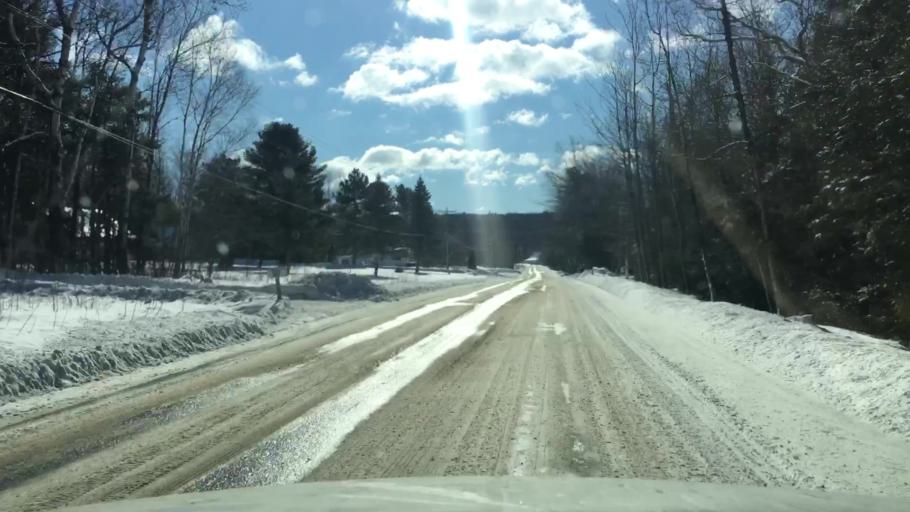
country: US
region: Maine
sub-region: Washington County
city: Calais
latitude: 45.0673
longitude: -67.4737
